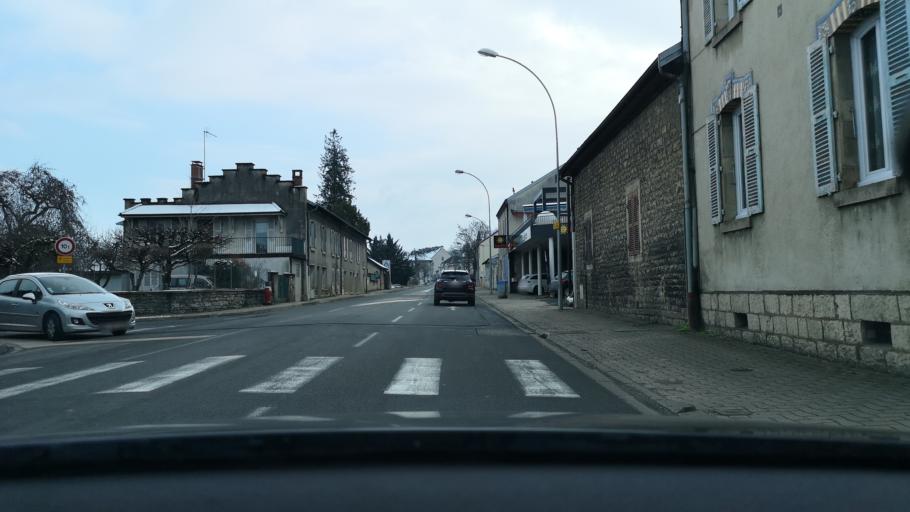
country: FR
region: Franche-Comte
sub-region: Departement du Jura
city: Montmorot
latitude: 46.6746
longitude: 5.5328
